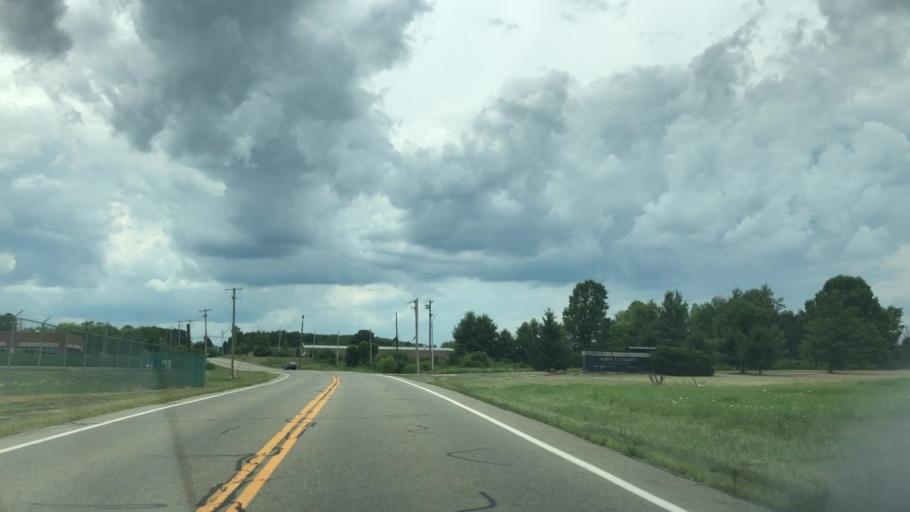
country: US
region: Ohio
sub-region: Summit County
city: Greensburg
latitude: 40.9300
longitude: -81.4423
